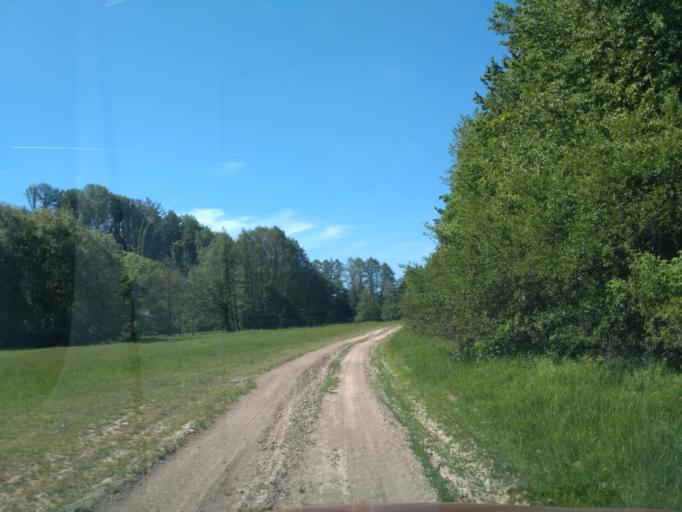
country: SK
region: Presovsky
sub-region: Okres Presov
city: Presov
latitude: 48.8887
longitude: 21.3928
